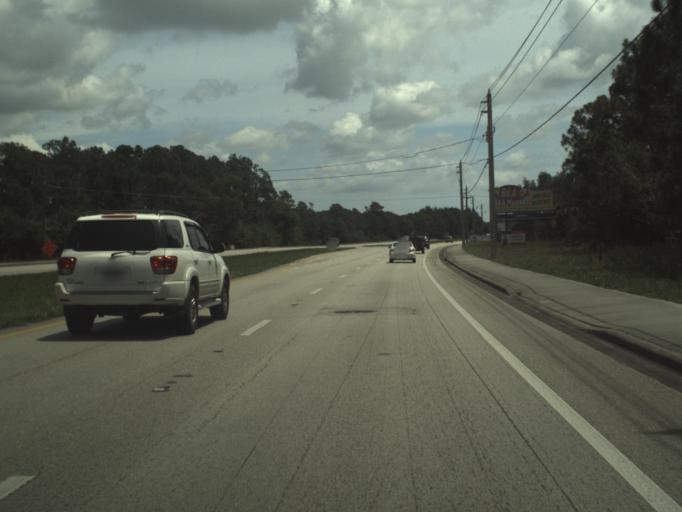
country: US
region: Florida
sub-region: Martin County
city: Palm City
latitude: 27.1310
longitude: -80.2513
